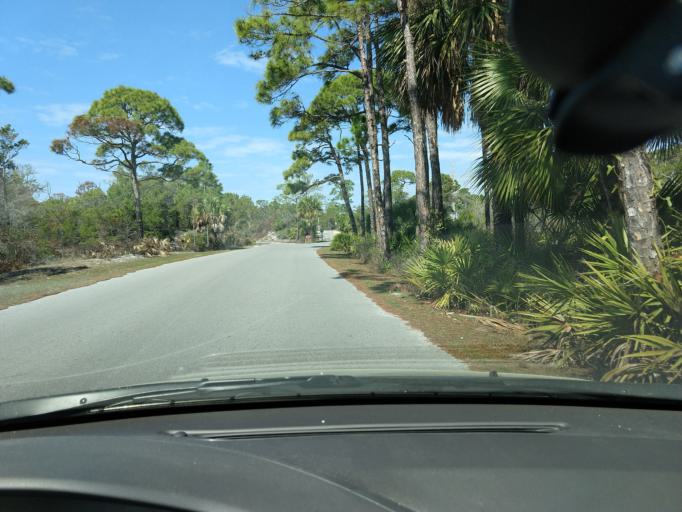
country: US
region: Florida
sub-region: Gulf County
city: Port Saint Joe
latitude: 29.7780
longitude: -85.4038
